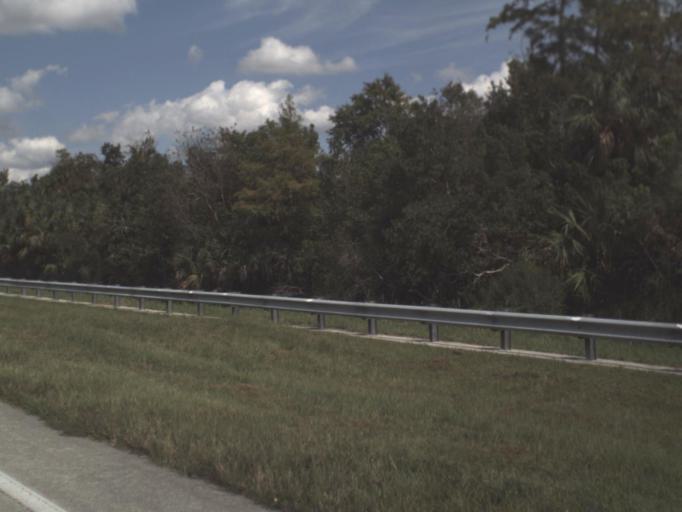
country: US
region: Florida
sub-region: Collier County
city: Orangetree
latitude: 26.1032
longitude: -81.3447
